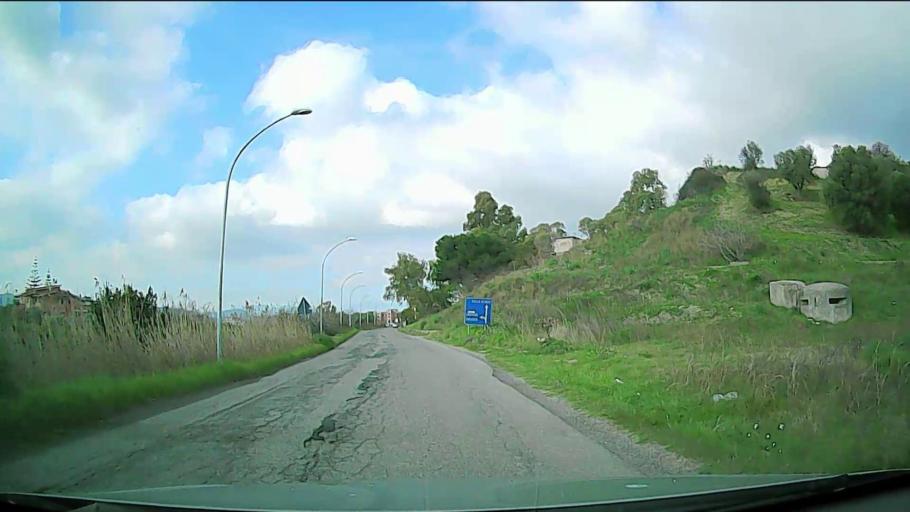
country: IT
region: Calabria
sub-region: Provincia di Crotone
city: Rocca di Neto
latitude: 39.1807
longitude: 17.0194
